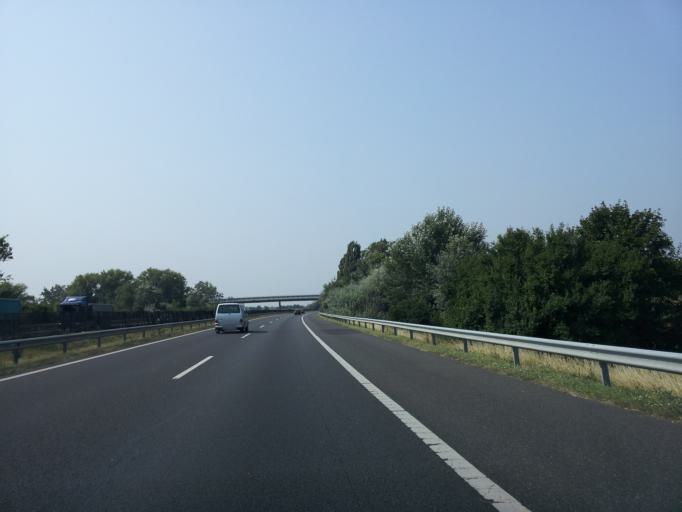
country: HU
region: Fejer
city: Kapolnasnyek
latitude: 47.2761
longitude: 18.7047
